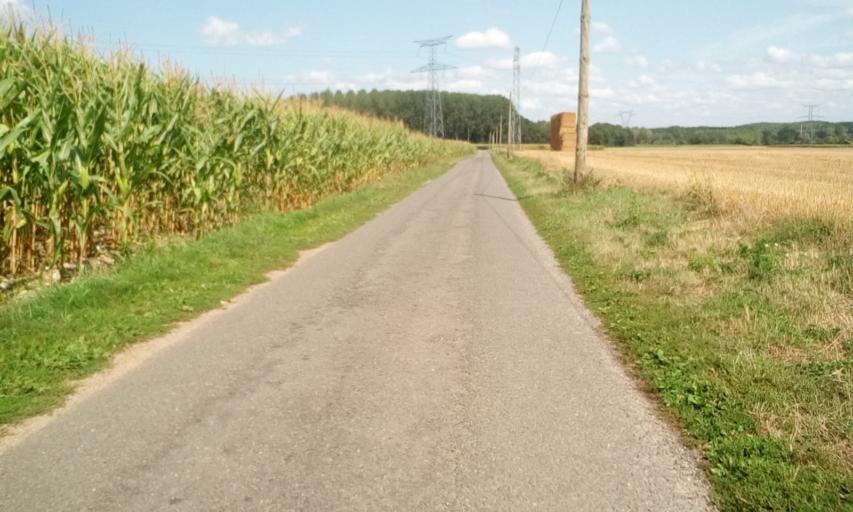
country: FR
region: Lower Normandy
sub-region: Departement du Calvados
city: Bellengreville
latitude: 49.1312
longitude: -0.1896
